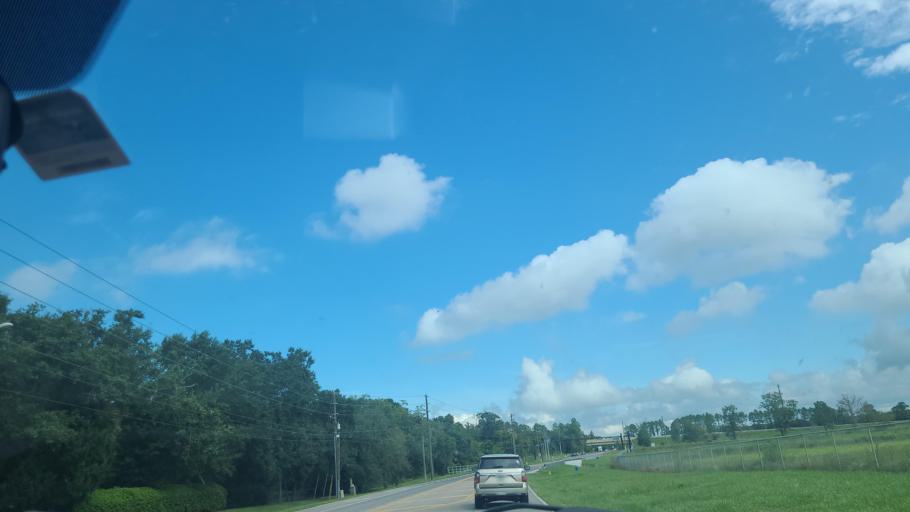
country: US
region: Florida
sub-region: Orange County
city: Ocoee
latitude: 28.5926
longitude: -81.5524
